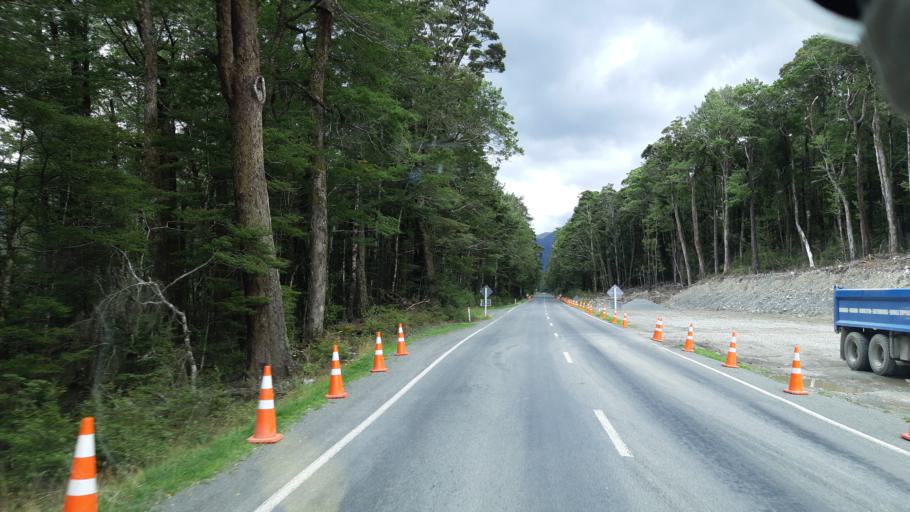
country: NZ
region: Canterbury
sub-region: Hurunui District
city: Amberley
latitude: -42.4901
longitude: 172.3874
